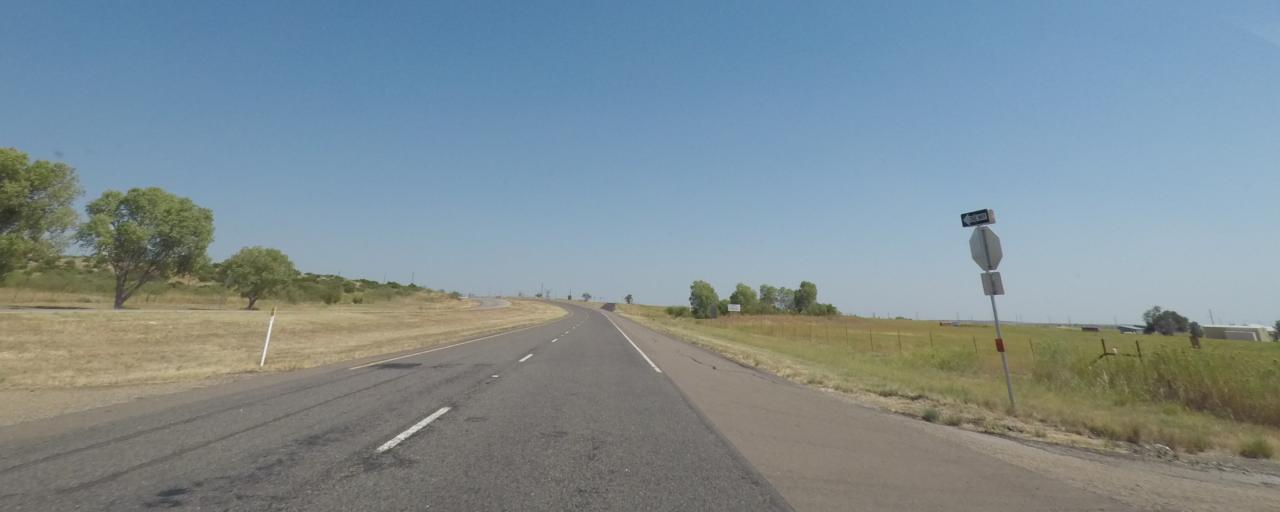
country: US
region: Texas
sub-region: Dickens County
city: Dickens
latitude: 33.6221
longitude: -100.8619
